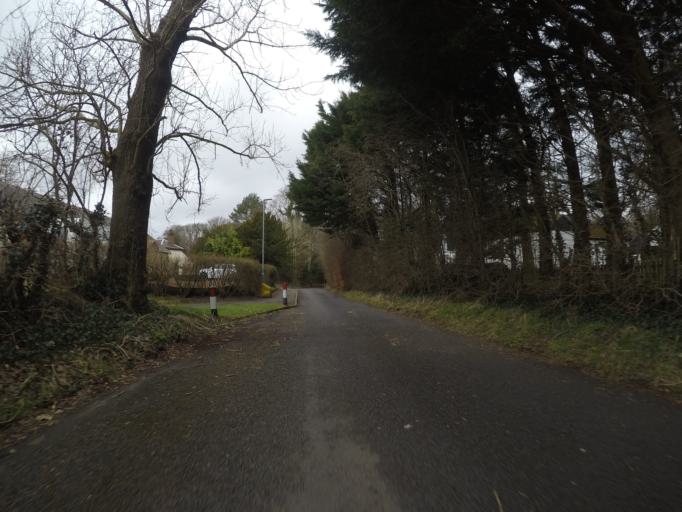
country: GB
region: Scotland
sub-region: North Ayrshire
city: Springside
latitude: 55.6302
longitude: -4.6192
